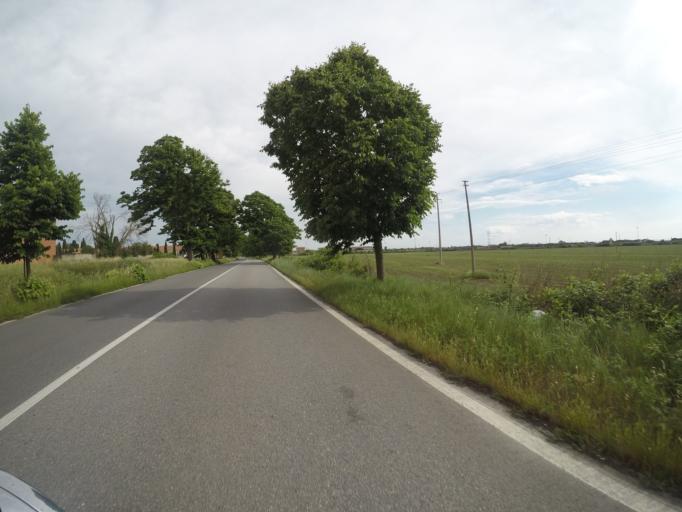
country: IT
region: Tuscany
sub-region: Province of Pisa
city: Madonna dell'Acqua
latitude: 43.7361
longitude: 10.3833
